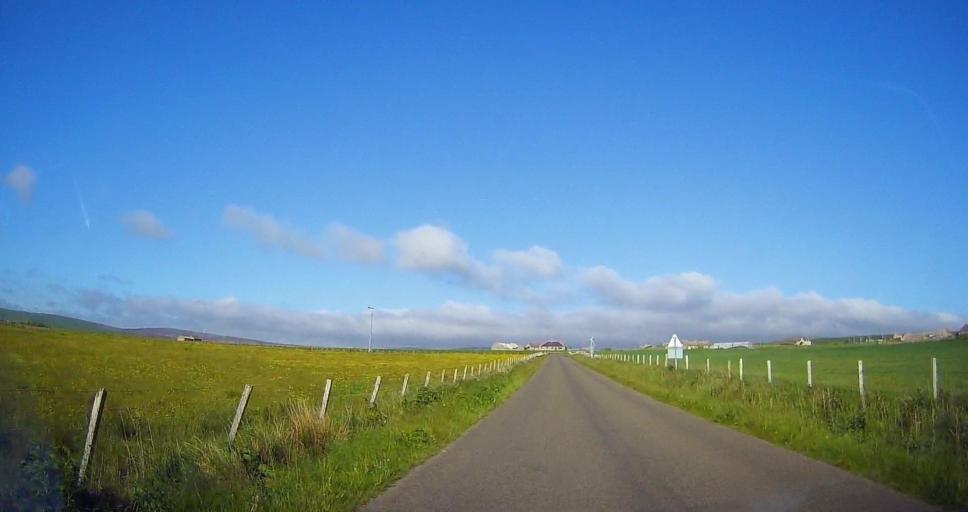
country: GB
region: Scotland
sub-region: Orkney Islands
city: Stromness
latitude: 59.0733
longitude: -3.2208
